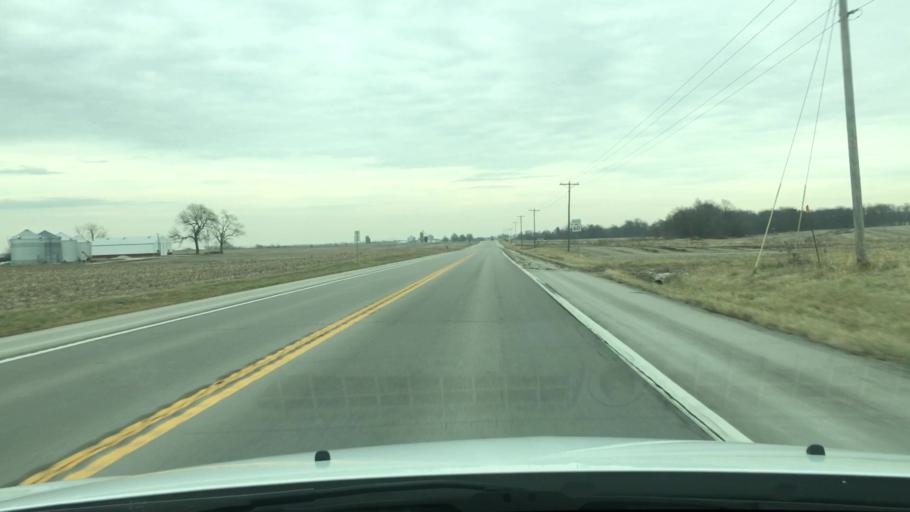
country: US
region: Missouri
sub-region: Audrain County
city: Mexico
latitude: 39.1642
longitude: -91.7208
